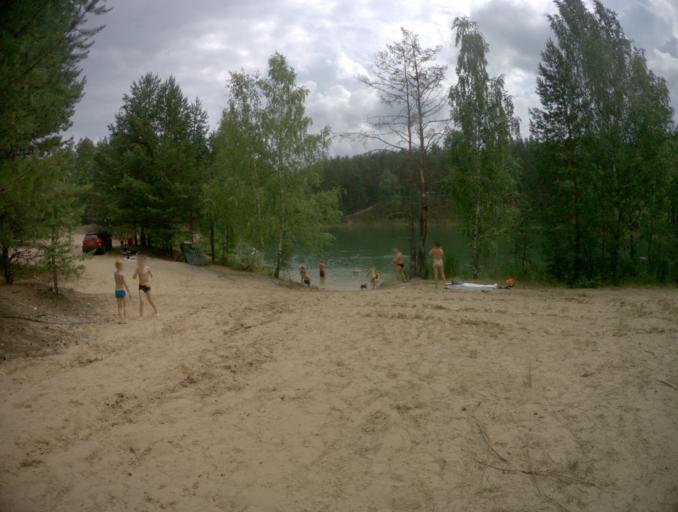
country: RU
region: Nizjnij Novgorod
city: Frolishchi
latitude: 56.3527
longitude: 42.7547
